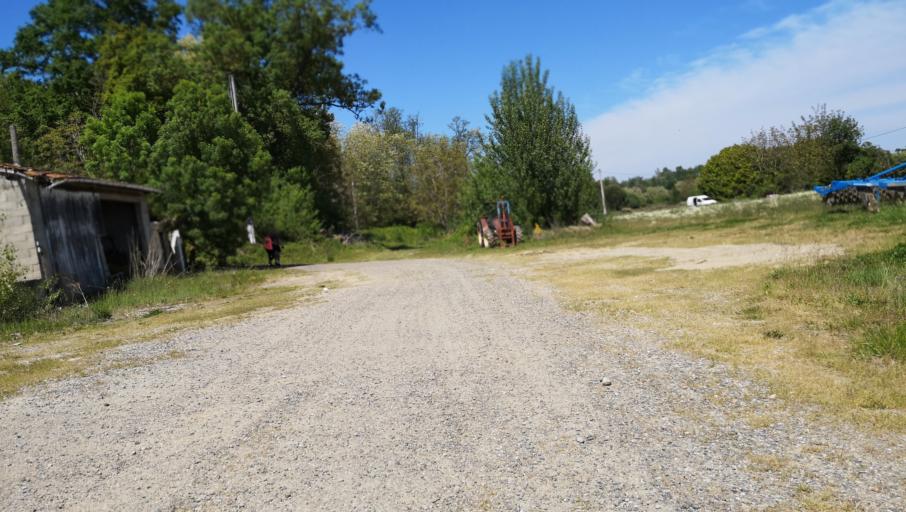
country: FR
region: Midi-Pyrenees
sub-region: Departement de la Haute-Garonne
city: Beauzelle
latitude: 43.6574
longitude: 1.3924
